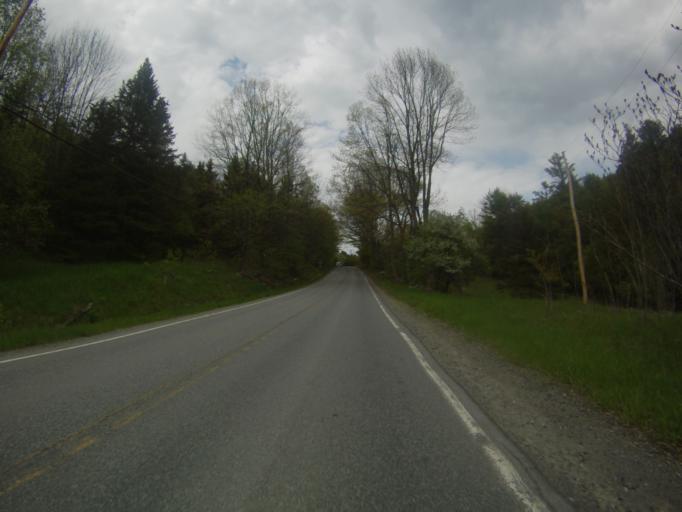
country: US
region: New York
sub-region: Essex County
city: Port Henry
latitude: 43.9611
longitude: -73.4889
